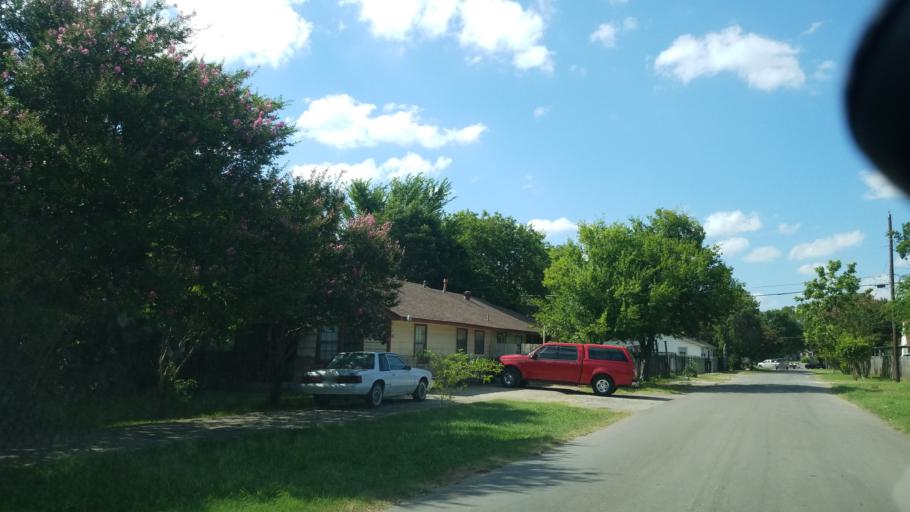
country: US
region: Texas
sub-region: Dallas County
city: Balch Springs
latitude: 32.7697
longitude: -96.7018
